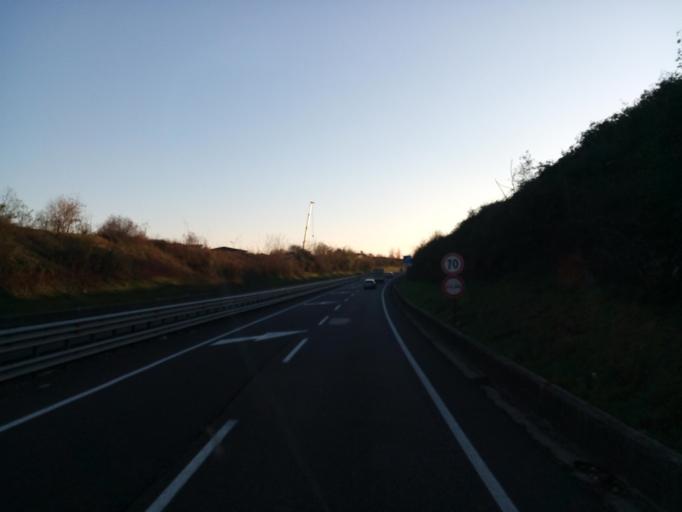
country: IT
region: Veneto
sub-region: Provincia di Vicenza
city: San Zeno-San Giuseppe
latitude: 45.7435
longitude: 11.7760
